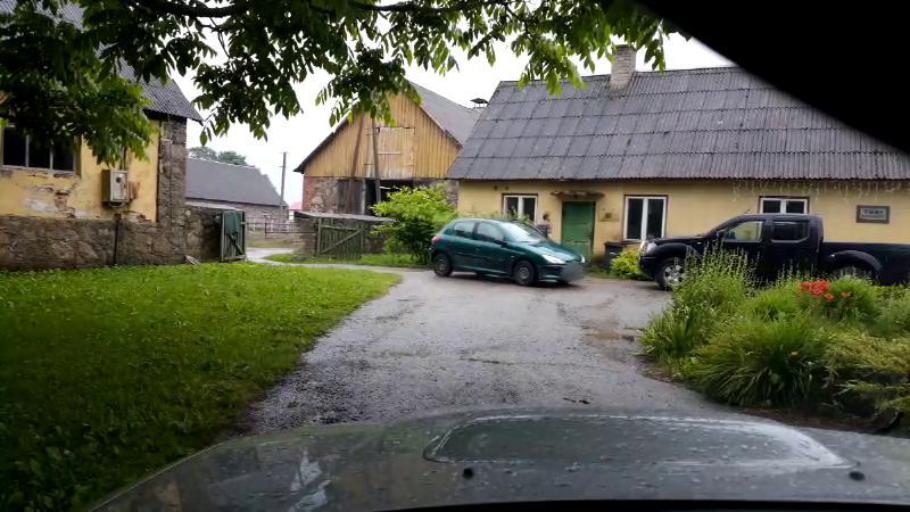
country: EE
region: Paernumaa
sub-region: Tootsi vald
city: Tootsi
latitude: 58.4804
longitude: 24.8112
